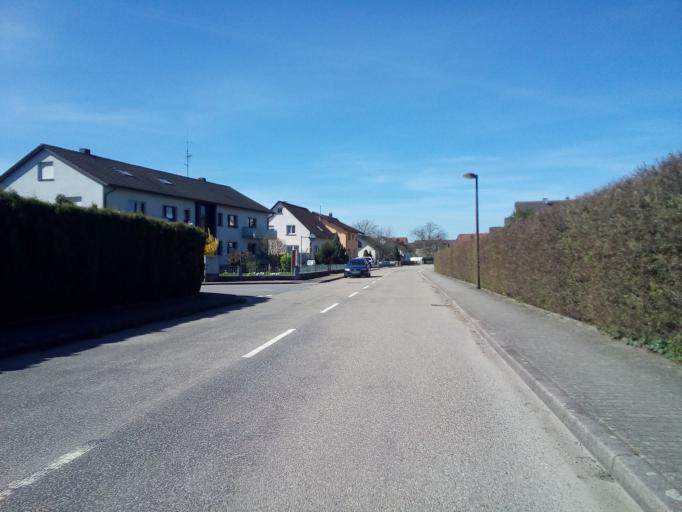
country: DE
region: Baden-Wuerttemberg
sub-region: Freiburg Region
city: Rheinau
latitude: 48.6519
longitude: 7.9320
